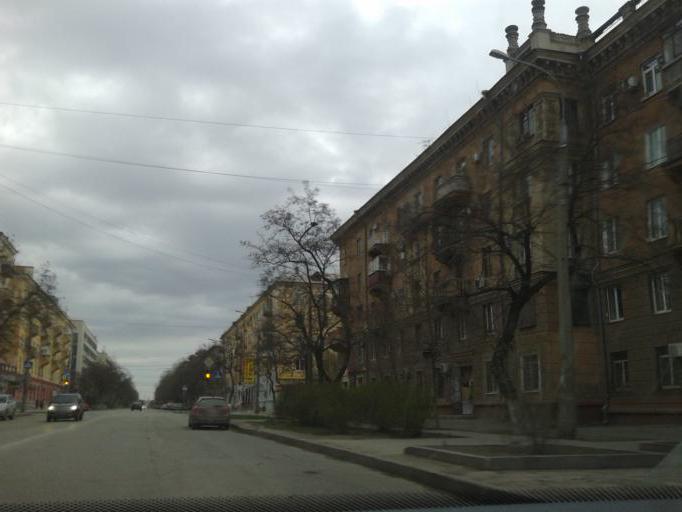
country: RU
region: Volgograd
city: Volgograd
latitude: 48.7111
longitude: 44.5276
